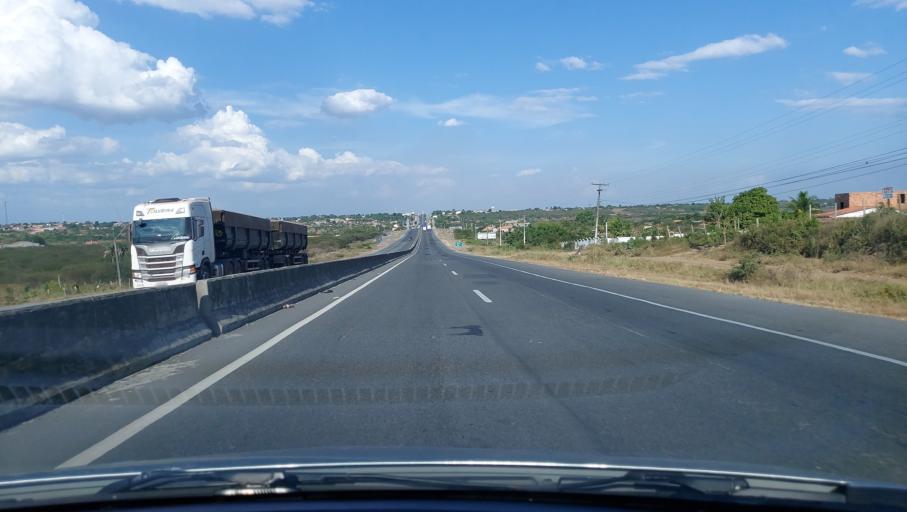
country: BR
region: Bahia
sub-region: Santo Estevao
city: Santo Estevao
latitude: -12.4578
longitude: -39.2649
